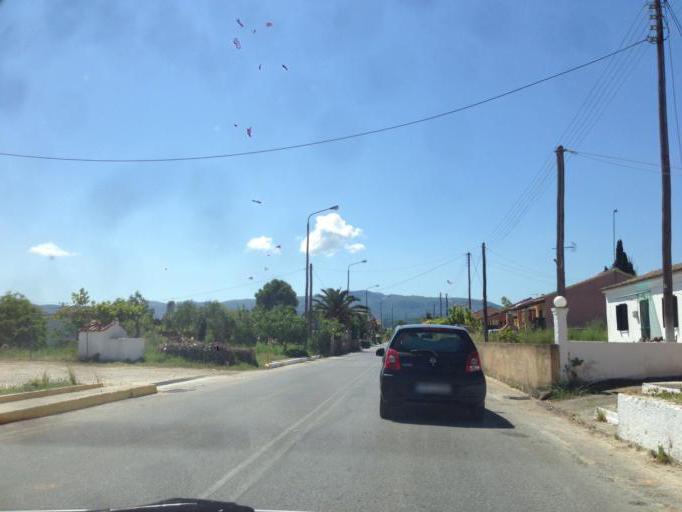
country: GR
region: Ionian Islands
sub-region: Nomos Kerkyras
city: Agios Georgis
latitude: 39.7686
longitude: 19.7155
